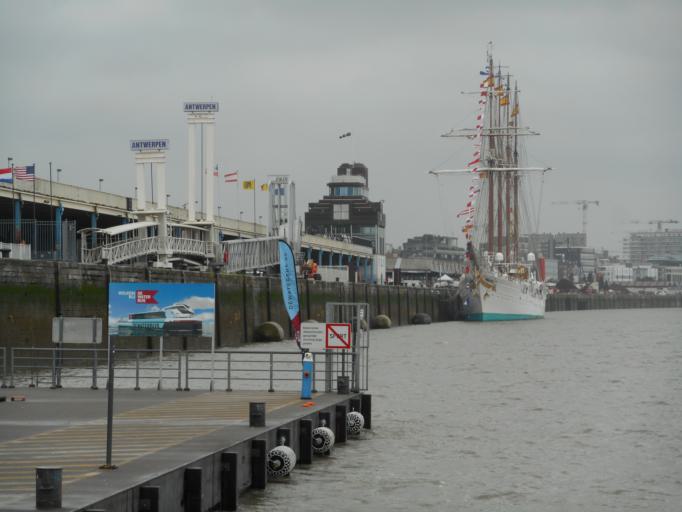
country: BE
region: Flanders
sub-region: Provincie Antwerpen
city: Antwerpen
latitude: 51.2224
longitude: 4.3961
